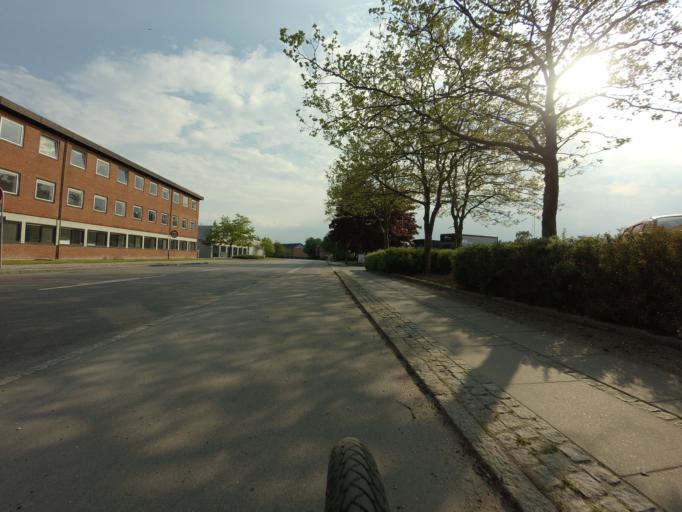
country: DK
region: Capital Region
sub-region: Glostrup Kommune
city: Glostrup
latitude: 55.6700
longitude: 12.4183
